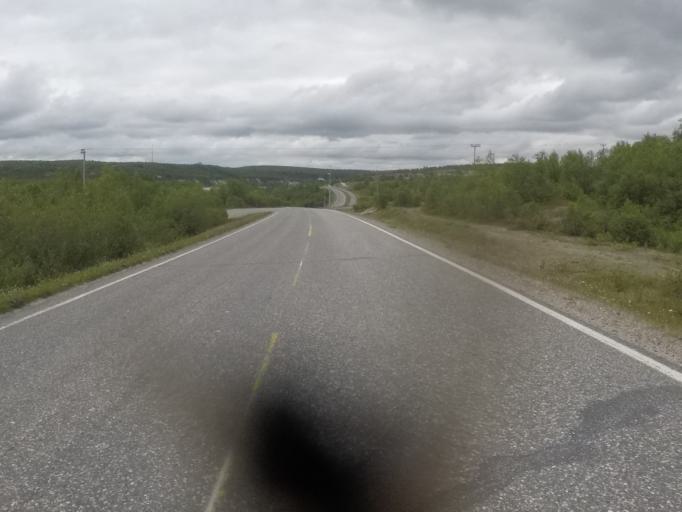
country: NO
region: Finnmark Fylke
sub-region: Kautokeino
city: Kautokeino
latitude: 68.9860
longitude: 23.0520
